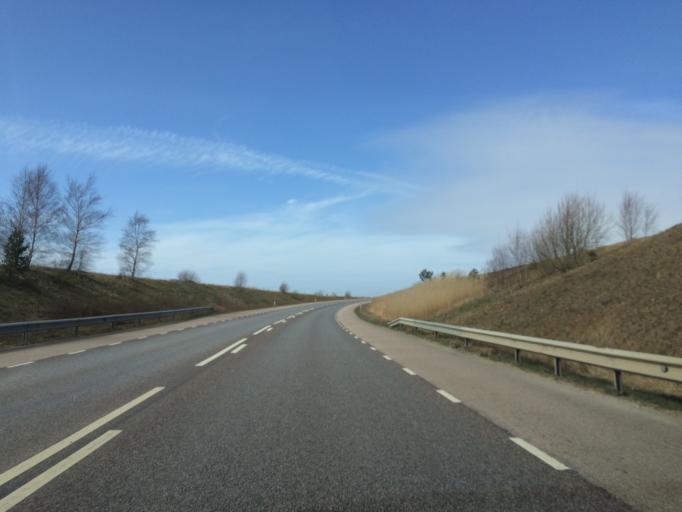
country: SE
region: Halland
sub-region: Laholms Kommun
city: Veinge
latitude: 56.5762
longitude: 13.0121
